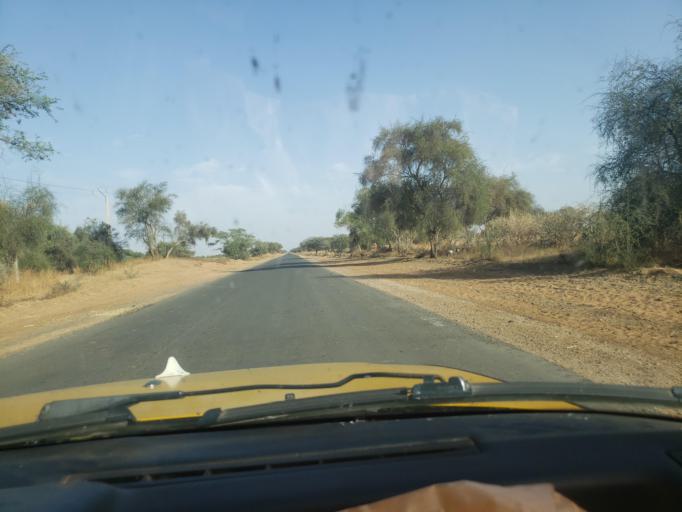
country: SN
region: Louga
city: Louga
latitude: 15.5083
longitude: -15.9732
